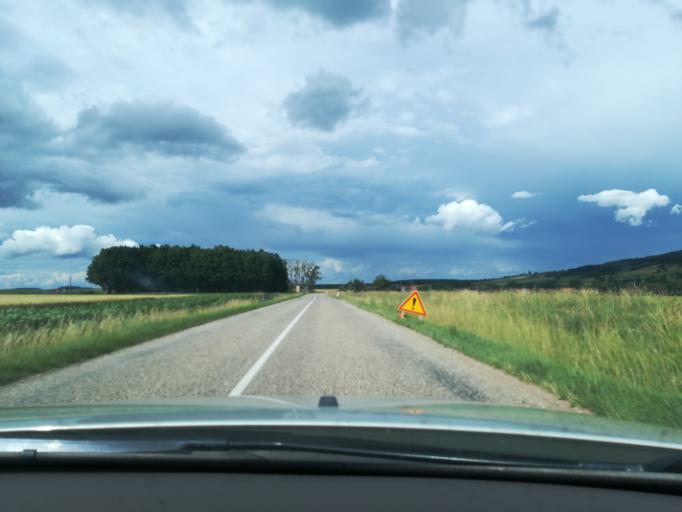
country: FR
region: Alsace
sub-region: Departement du Bas-Rhin
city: Dossenheim-sur-Zinsel
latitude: 48.8109
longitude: 7.4246
